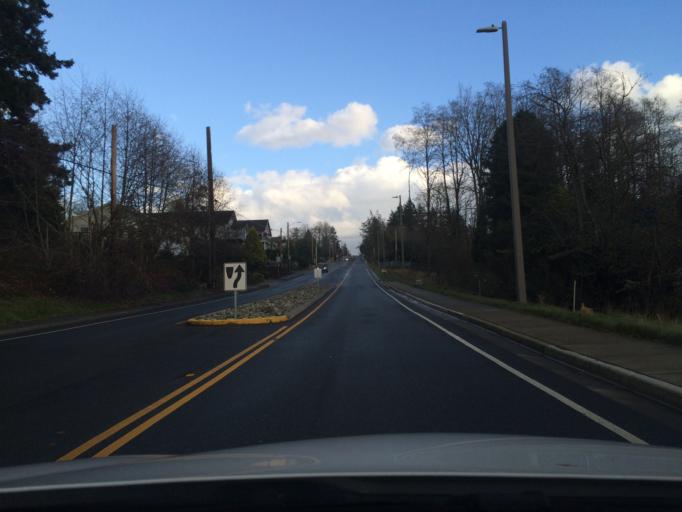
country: US
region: Washington
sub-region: Whatcom County
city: Blaine
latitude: 48.9940
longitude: -122.7281
